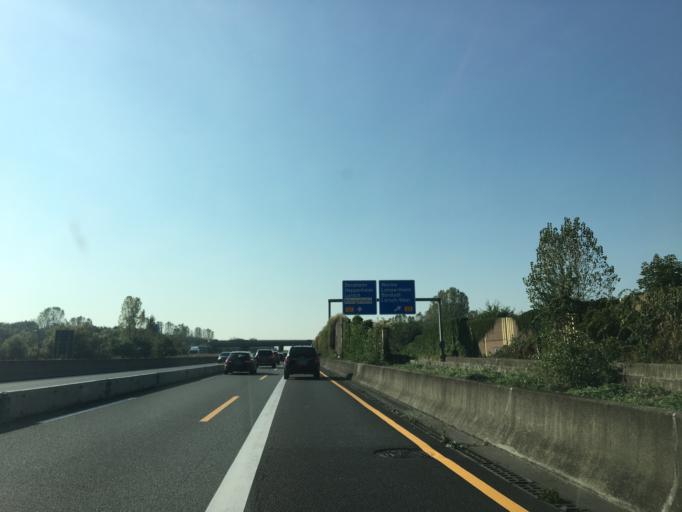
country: DE
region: Hesse
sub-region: Regierungsbezirk Darmstadt
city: Einhausen
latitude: 49.6638
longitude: 8.5548
